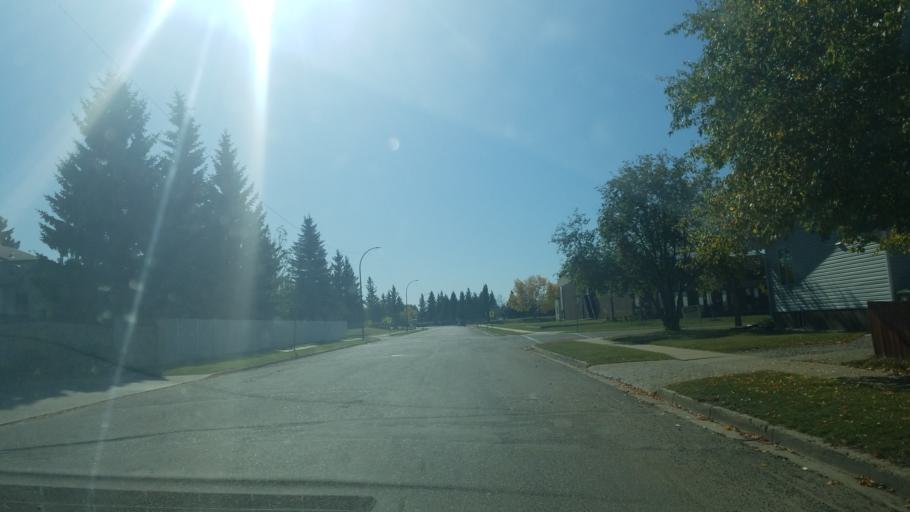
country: CA
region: Saskatchewan
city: Lloydminster
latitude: 53.2764
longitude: -110.0198
